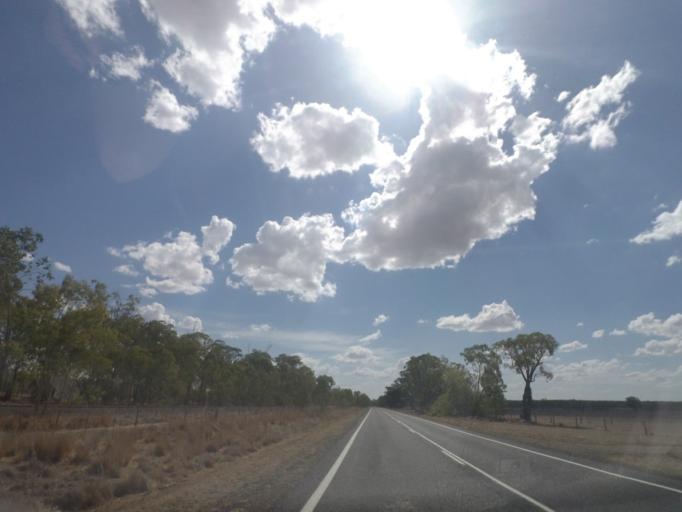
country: AU
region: Queensland
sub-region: Southern Downs
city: Stanthorpe
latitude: -28.3944
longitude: 151.3121
